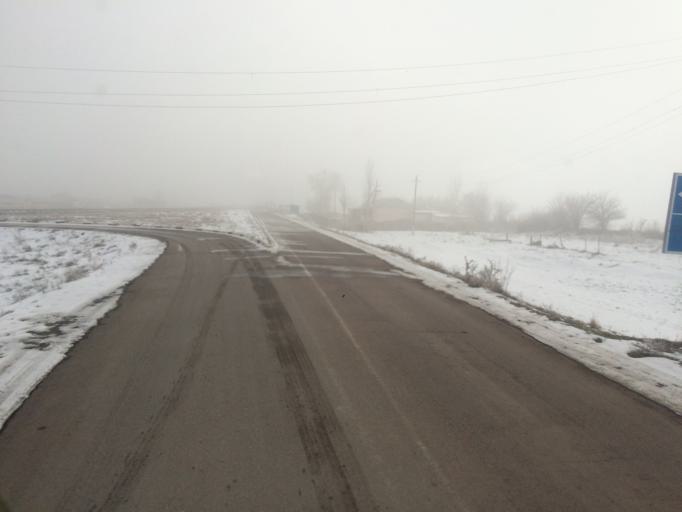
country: KZ
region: Zhambyl
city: Merke
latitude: 42.9131
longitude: 73.1621
